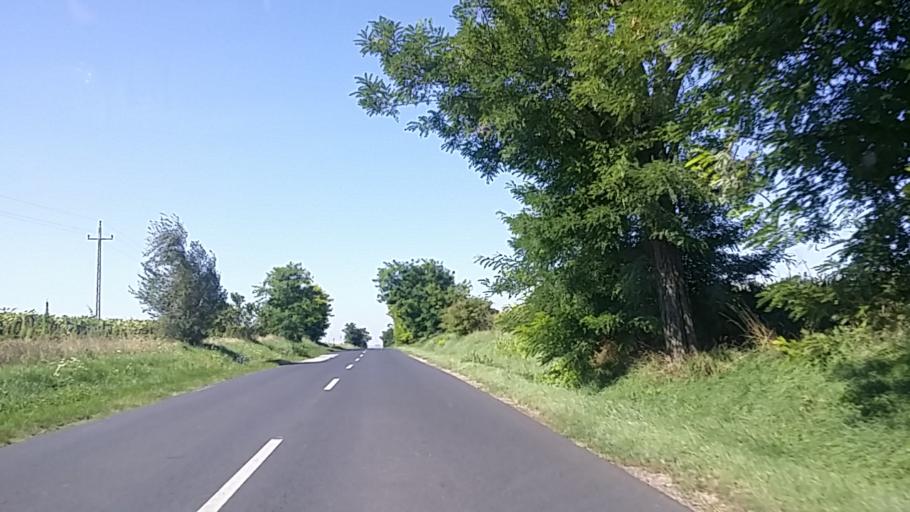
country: HU
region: Fejer
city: Sarbogard
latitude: 46.8843
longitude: 18.6879
